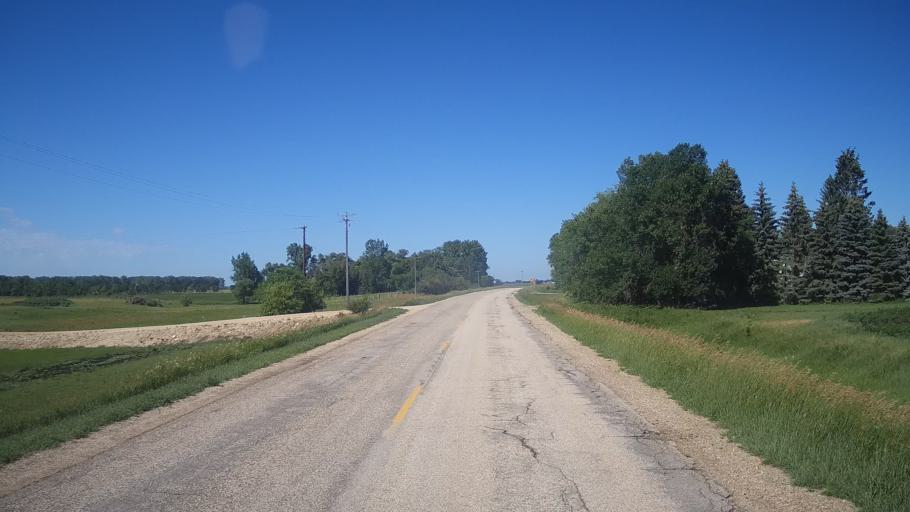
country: CA
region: Manitoba
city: Portage la Prairie
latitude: 50.0449
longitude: -98.0267
